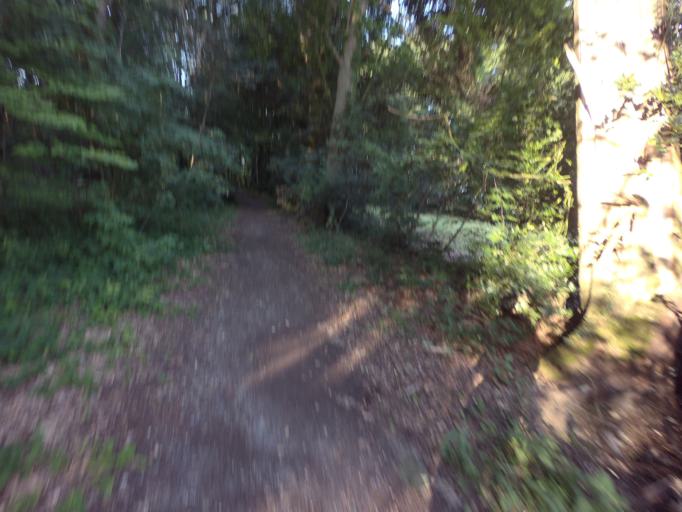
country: BE
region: Flanders
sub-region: Provincie Limburg
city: Sint-Pieters-Voeren
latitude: 50.7683
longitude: 5.8893
